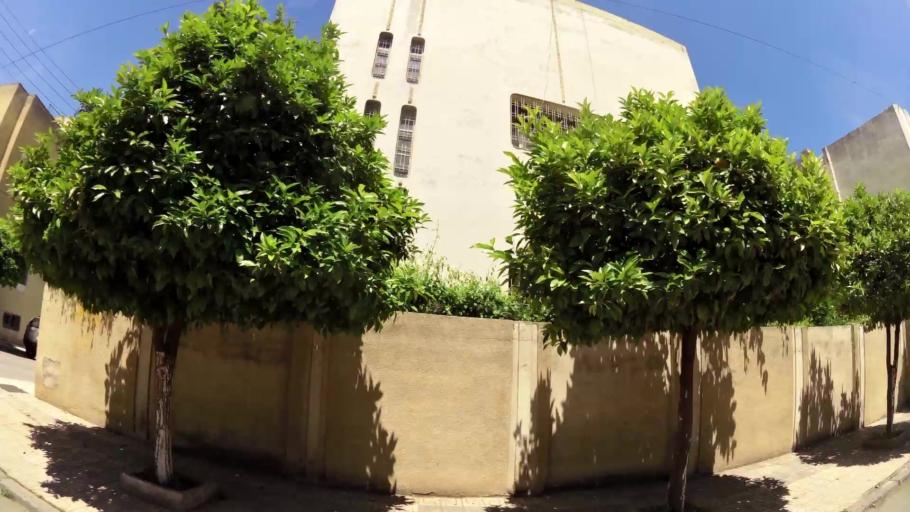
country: MA
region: Fes-Boulemane
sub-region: Fes
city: Fes
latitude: 34.0172
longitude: -5.0103
